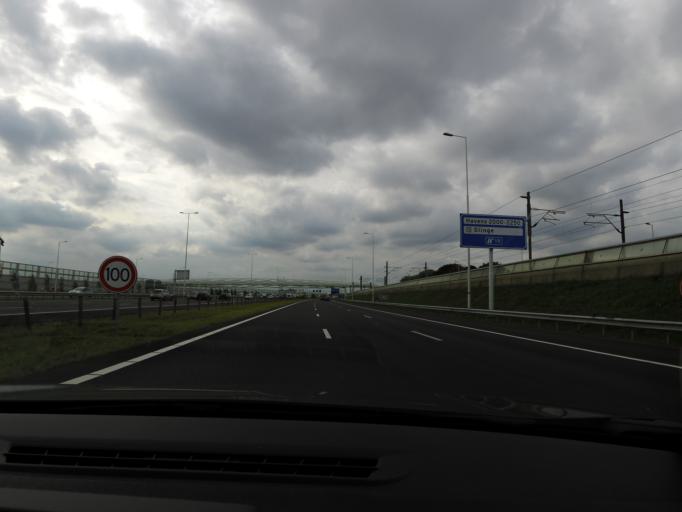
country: NL
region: South Holland
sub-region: Gemeente Binnenmaas
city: Heinenoord
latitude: 51.8623
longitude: 4.4692
